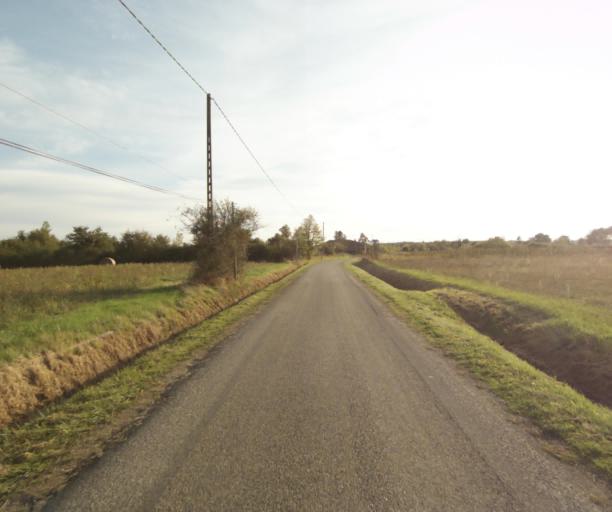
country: FR
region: Midi-Pyrenees
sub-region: Departement du Tarn-et-Garonne
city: Campsas
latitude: 43.8808
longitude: 1.3514
